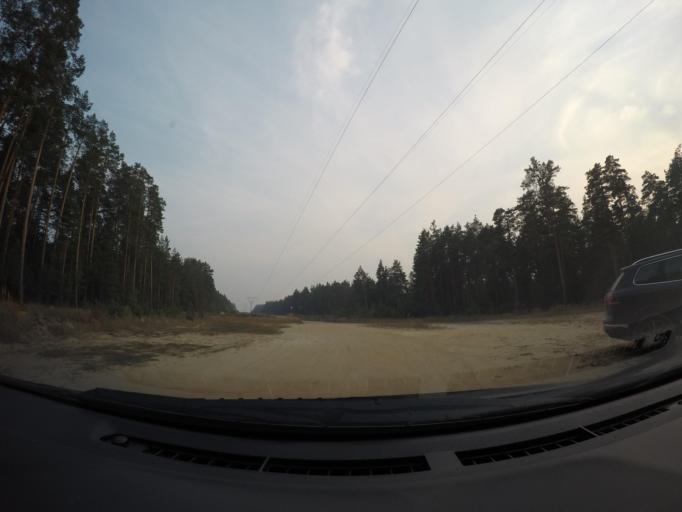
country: RU
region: Moskovskaya
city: Imeni Tsyurupy
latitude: 55.4976
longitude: 38.6883
